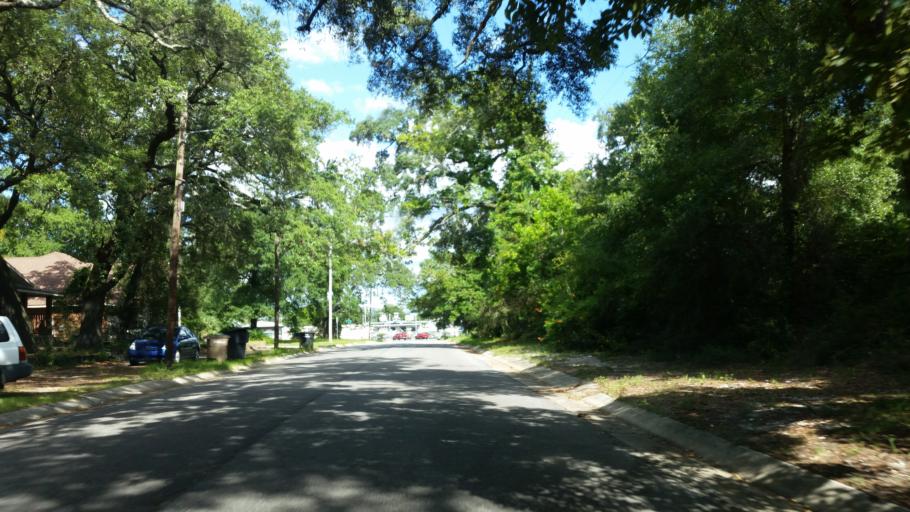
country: US
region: Florida
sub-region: Escambia County
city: Pensacola
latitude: 30.4024
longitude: -87.2445
